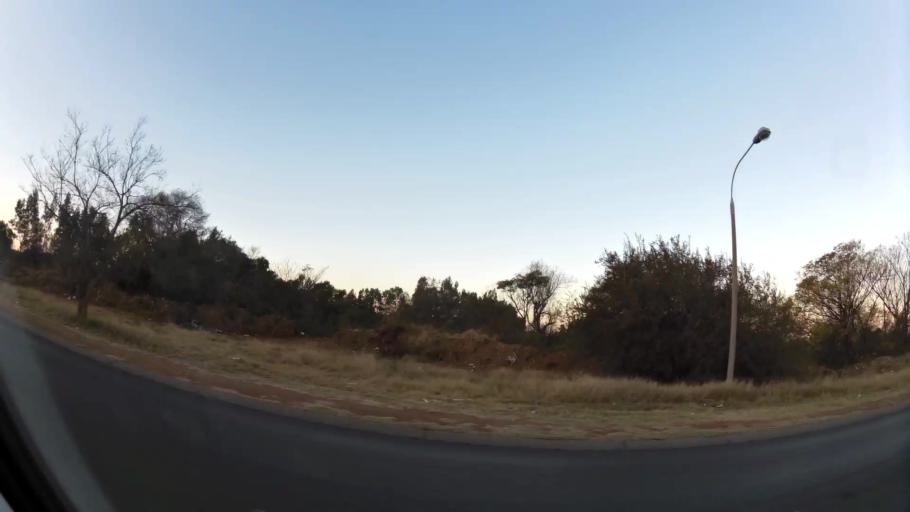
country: ZA
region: North-West
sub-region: Bojanala Platinum District Municipality
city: Rustenburg
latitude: -25.6686
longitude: 27.2167
